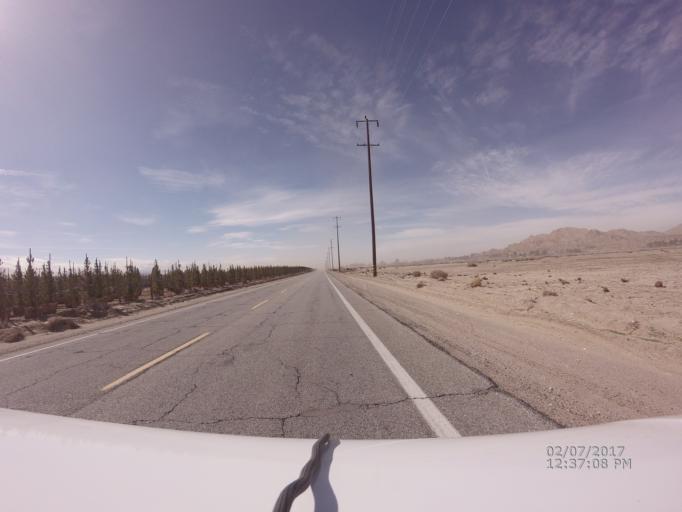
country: US
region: California
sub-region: Los Angeles County
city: Lake Los Angeles
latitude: 34.5799
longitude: -117.8381
